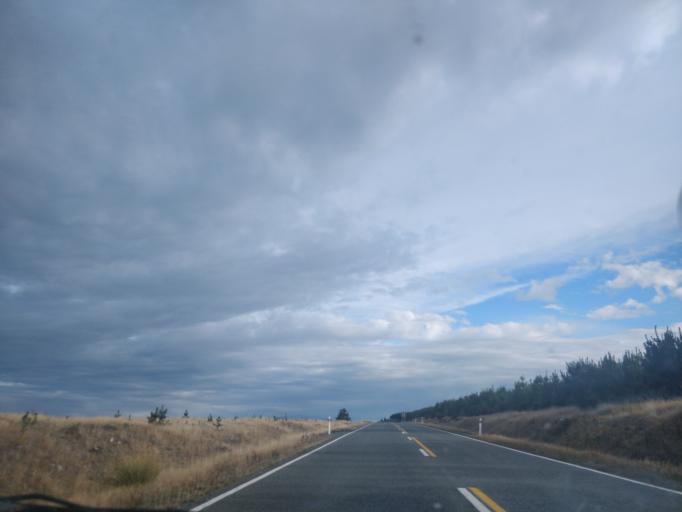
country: NZ
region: Canterbury
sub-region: Timaru District
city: Pleasant Point
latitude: -44.0911
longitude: 170.1348
